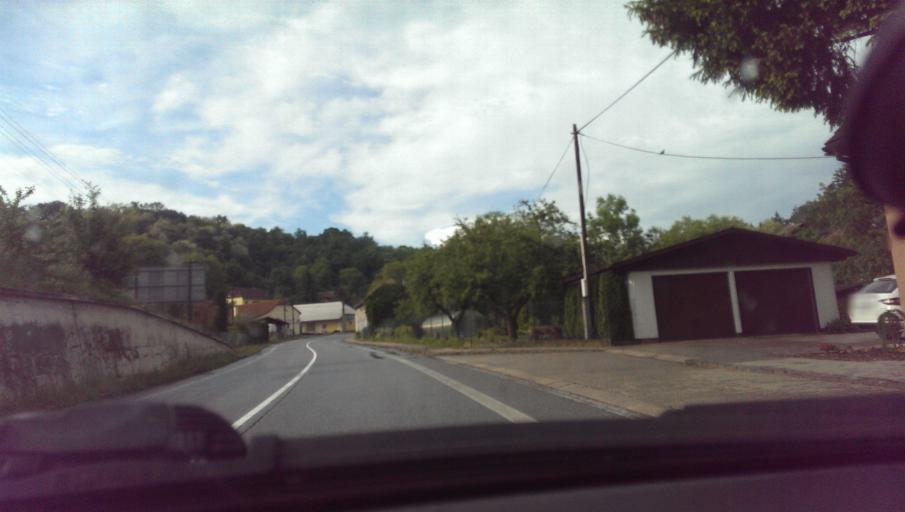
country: CZ
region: Zlin
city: Brezolupy
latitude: 49.1451
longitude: 17.6055
